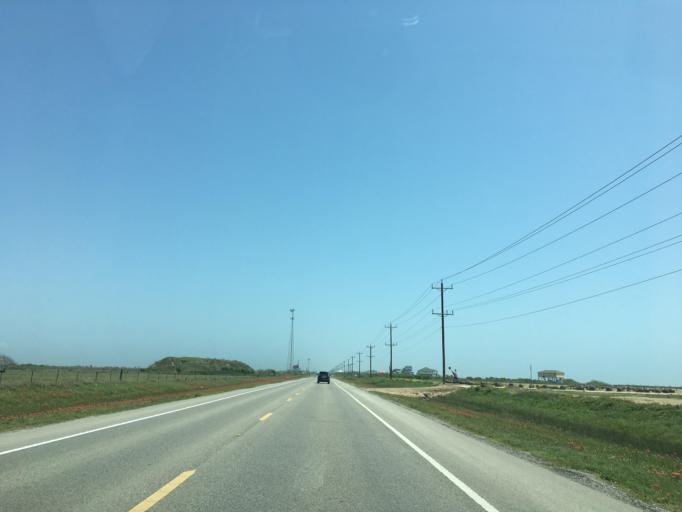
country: US
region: Texas
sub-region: Galveston County
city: Bolivar Peninsula
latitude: 29.4890
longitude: -94.5534
